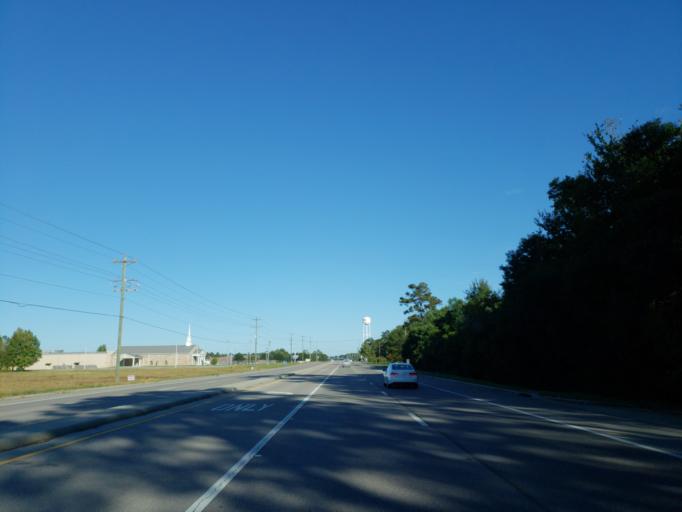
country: US
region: Mississippi
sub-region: Forrest County
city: Petal
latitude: 31.3503
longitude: -89.2109
